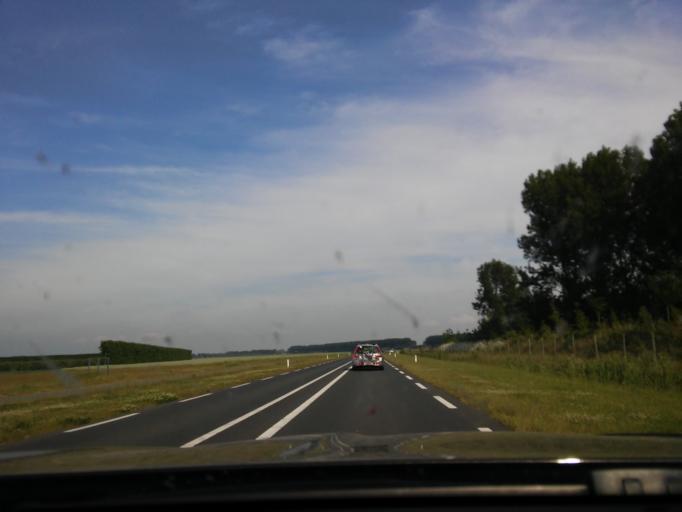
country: BE
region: Flanders
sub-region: Provincie Oost-Vlaanderen
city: Maldegem
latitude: 51.2774
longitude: 3.4591
